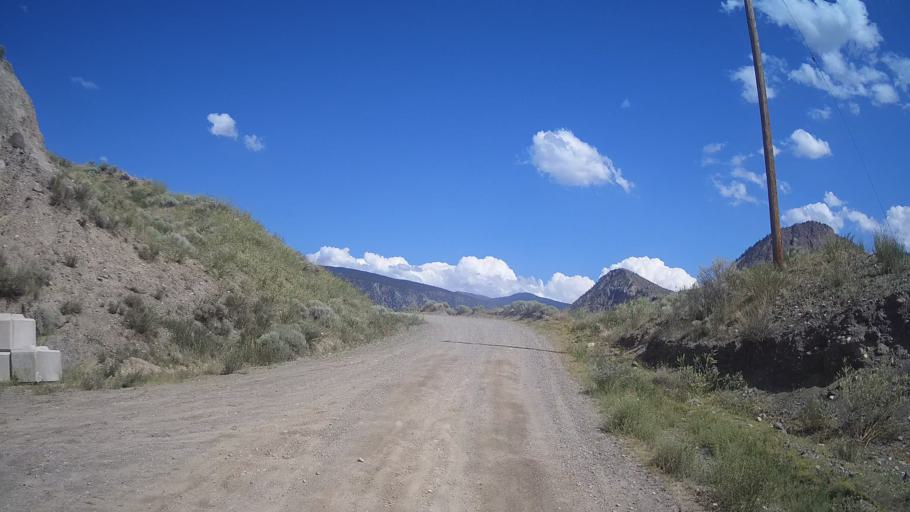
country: CA
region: British Columbia
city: Lillooet
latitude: 51.1814
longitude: -122.1257
